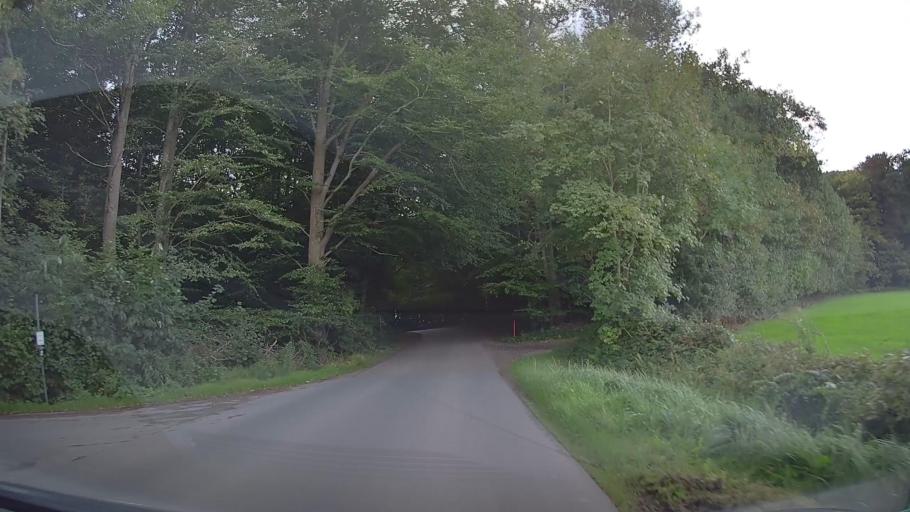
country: DE
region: Schleswig-Holstein
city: Steinberg
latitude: 54.7870
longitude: 9.7796
